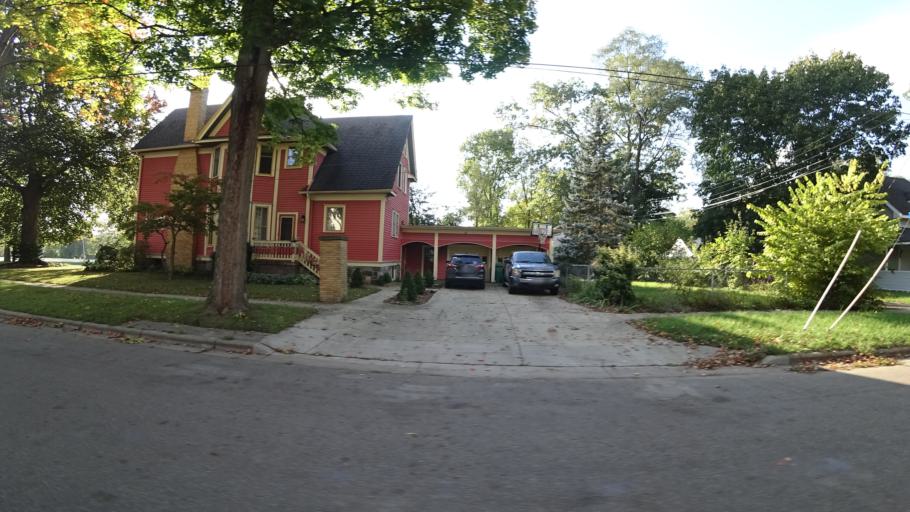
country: US
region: Michigan
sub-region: Saint Joseph County
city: Three Rivers
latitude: 41.9450
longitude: -85.6287
